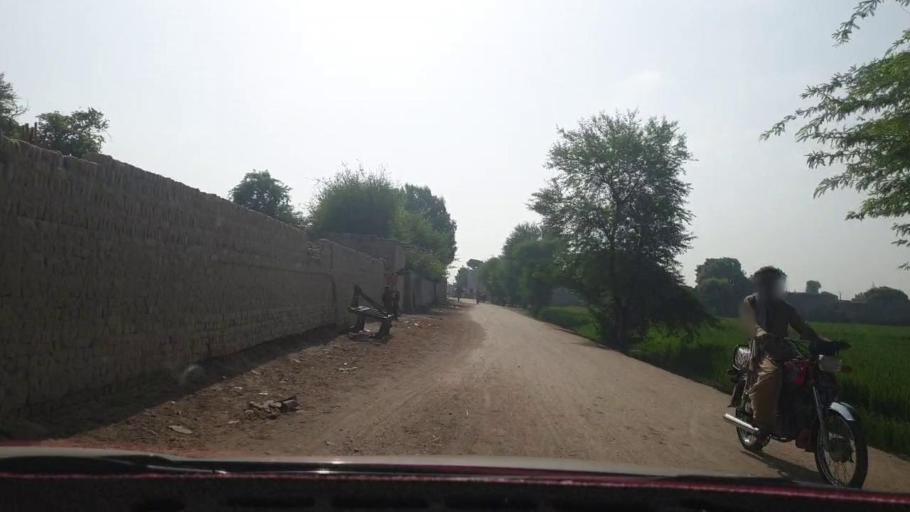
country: PK
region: Sindh
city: Nasirabad
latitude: 27.4437
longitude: 67.9436
